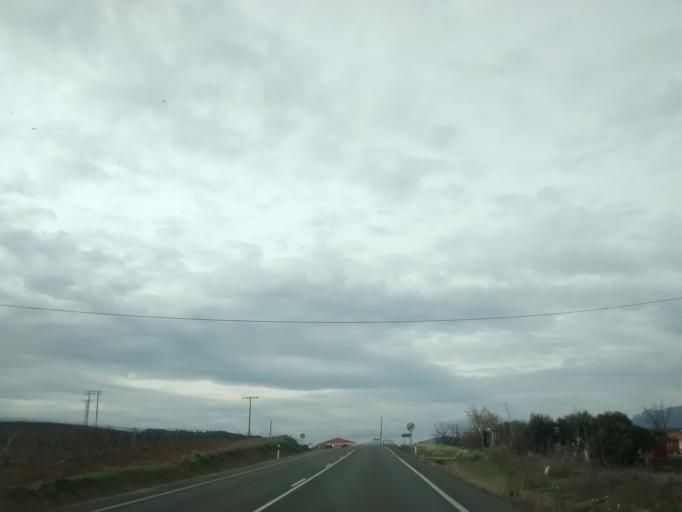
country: ES
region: La Rioja
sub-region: Provincia de La Rioja
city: Torremontalbo
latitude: 42.4946
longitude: -2.6702
